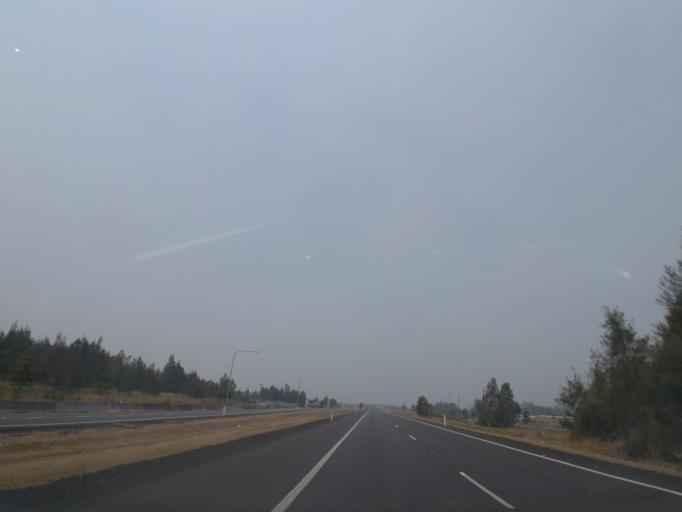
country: AU
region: New South Wales
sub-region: Ballina
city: Ballina
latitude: -28.8632
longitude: 153.5133
